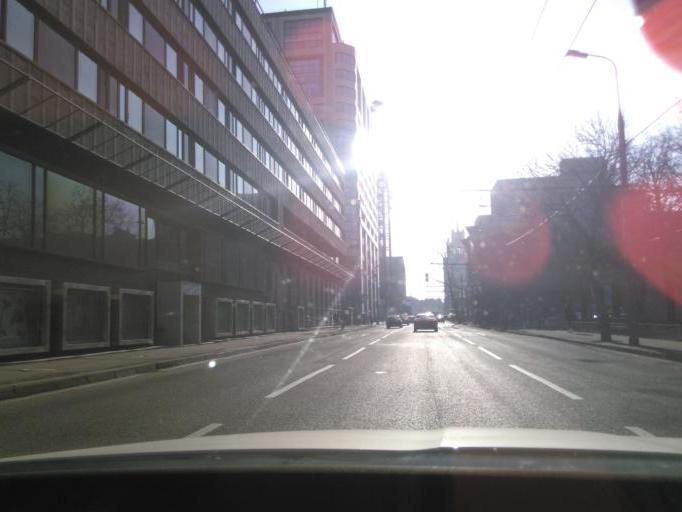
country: RU
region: Moskovskaya
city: Dorogomilovo
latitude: 55.7719
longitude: 37.5889
